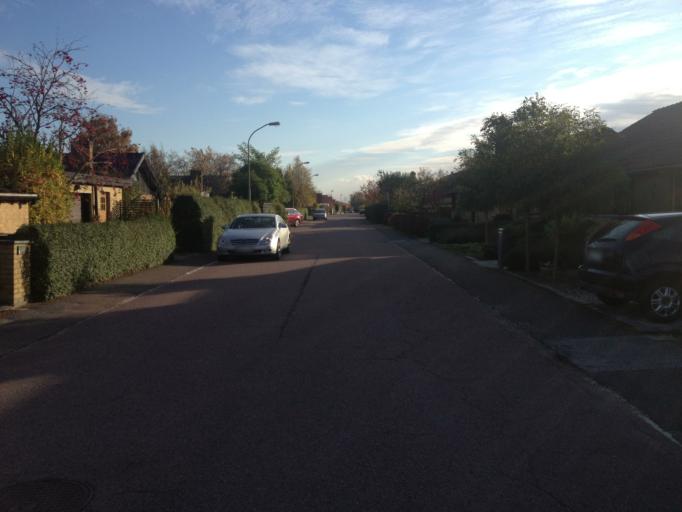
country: SE
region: Skane
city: Bjarred
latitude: 55.7229
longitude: 13.0359
